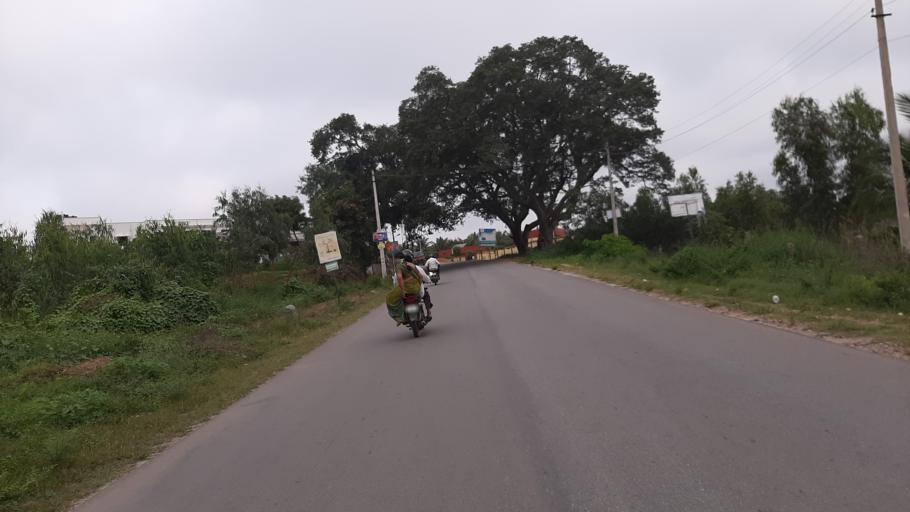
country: IN
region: Karnataka
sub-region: Bangalore Rural
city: Nelamangala
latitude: 12.9666
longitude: 77.3907
